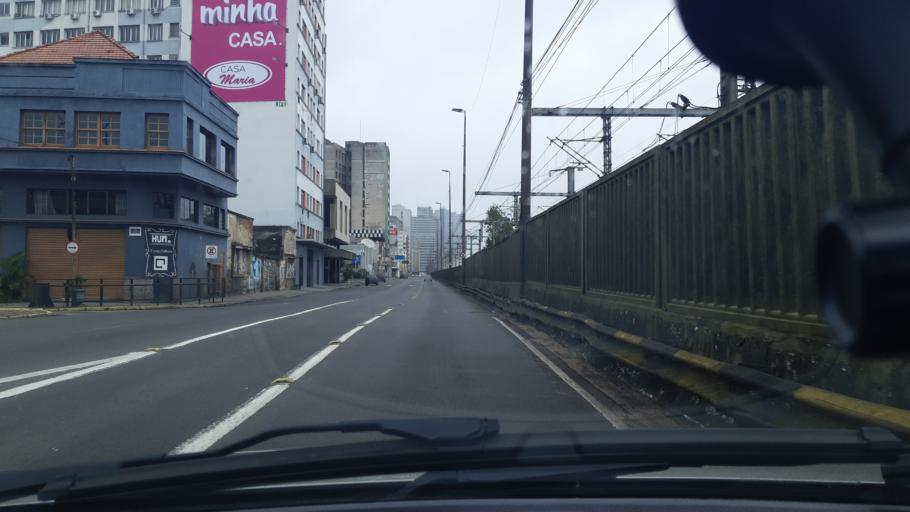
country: BR
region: Rio Grande do Sul
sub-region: Porto Alegre
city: Porto Alegre
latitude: -30.0231
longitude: -51.2209
